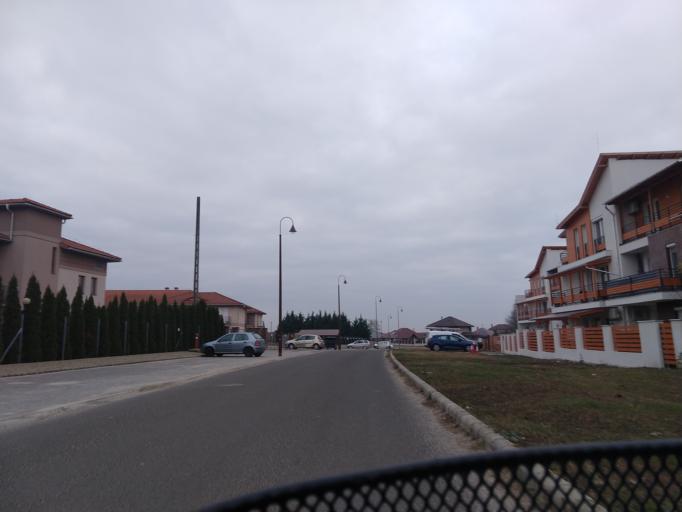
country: HU
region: Pest
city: Orbottyan
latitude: 47.6586
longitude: 19.2567
